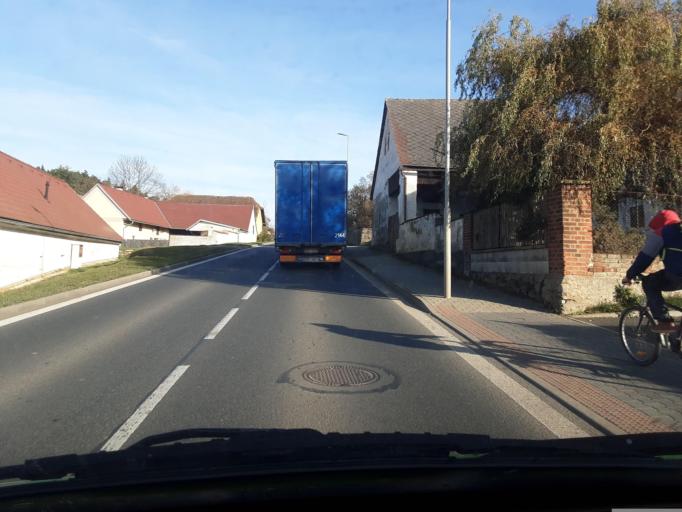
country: CZ
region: Plzensky
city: Horazd'ovice
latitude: 49.3306
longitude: 13.6524
